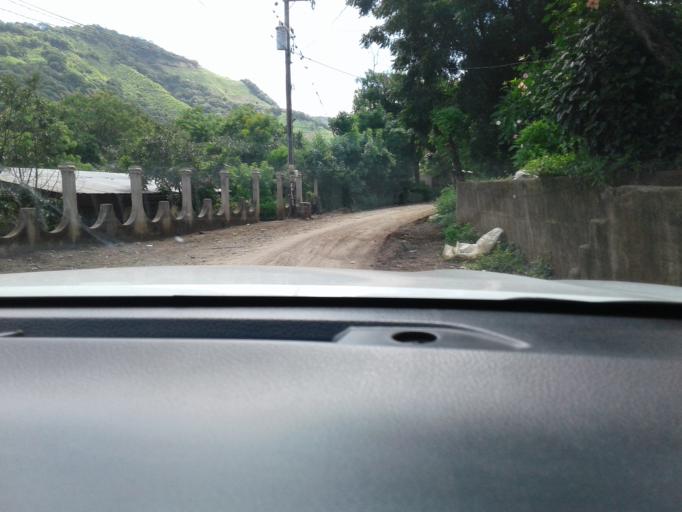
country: NI
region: Matagalpa
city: Terrabona
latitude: 12.8346
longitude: -85.9925
